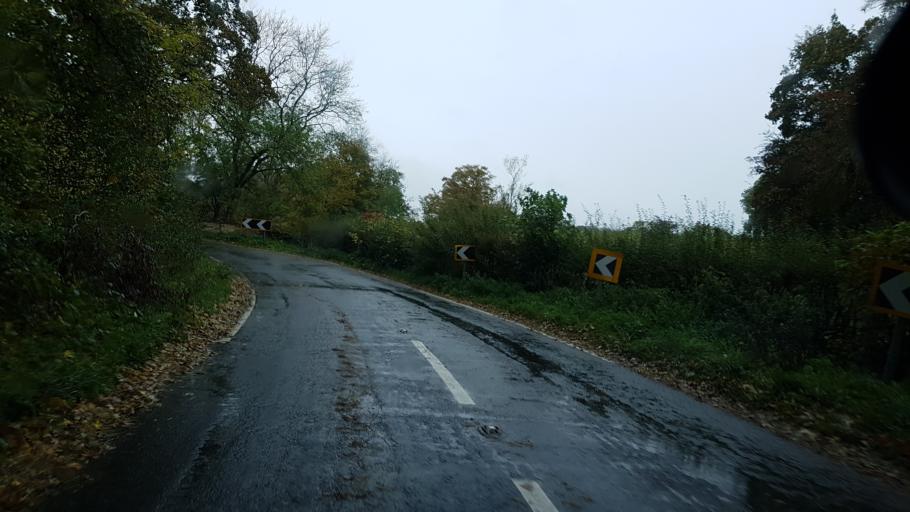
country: GB
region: England
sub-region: Gloucestershire
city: Stow on the Wold
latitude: 51.9393
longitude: -1.7418
